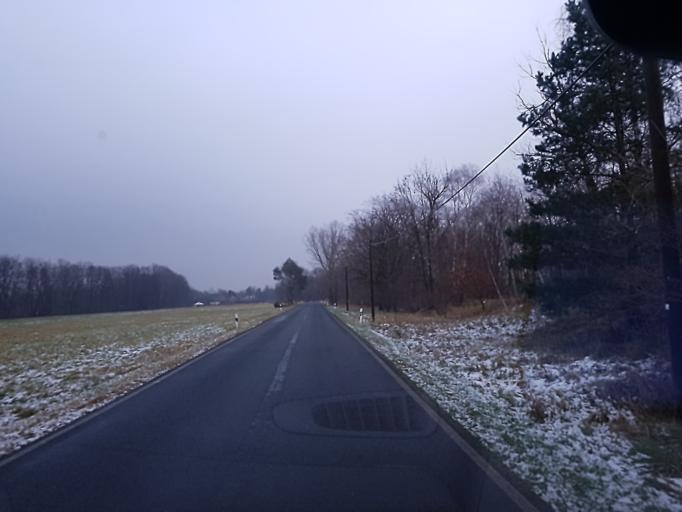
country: DE
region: Brandenburg
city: Lubbenau
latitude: 51.8238
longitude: 13.9135
